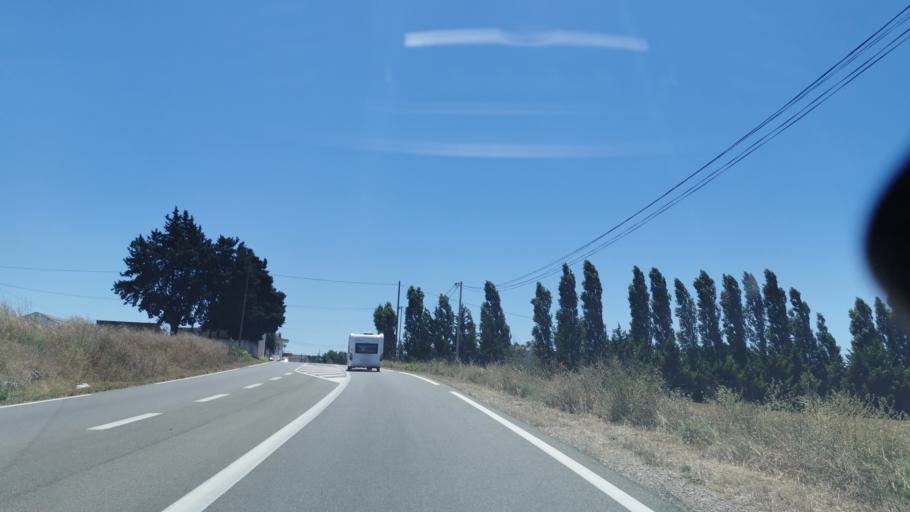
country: FR
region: Languedoc-Roussillon
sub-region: Departement de l'Herault
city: Beziers
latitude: 43.3197
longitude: 3.1856
